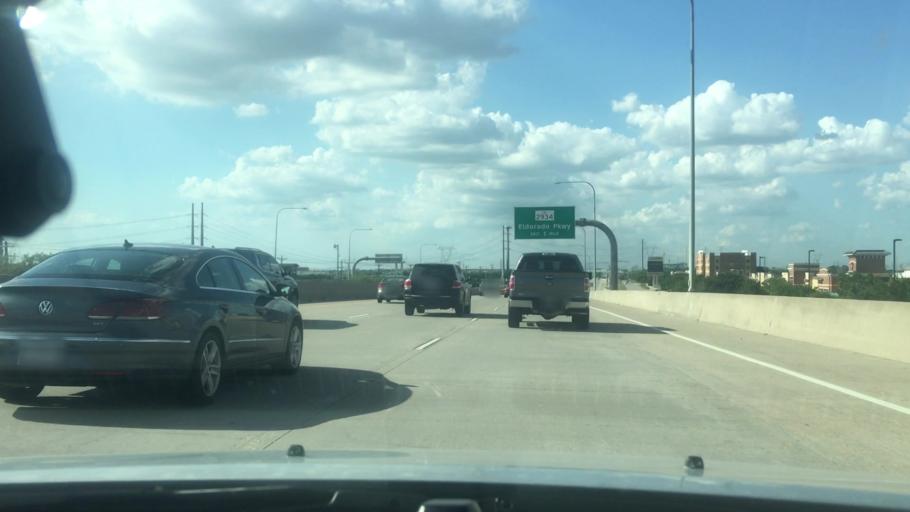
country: US
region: Texas
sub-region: Collin County
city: Frisco
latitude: 33.1538
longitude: -96.8400
